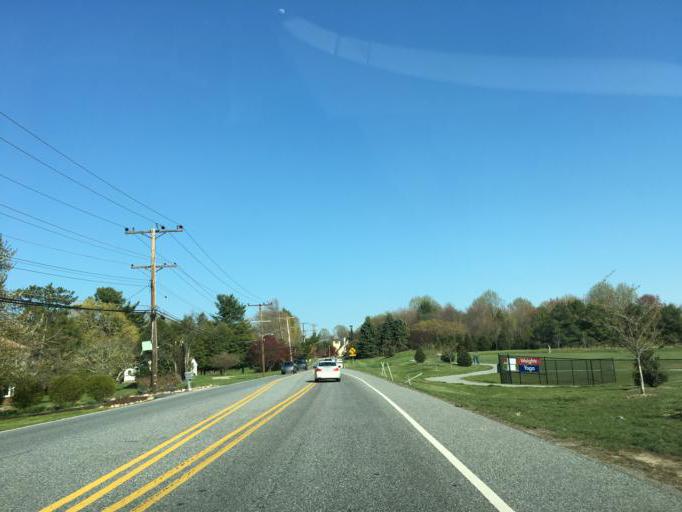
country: US
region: Maryland
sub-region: Baltimore County
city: Hunt Valley
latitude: 39.5138
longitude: -76.5541
